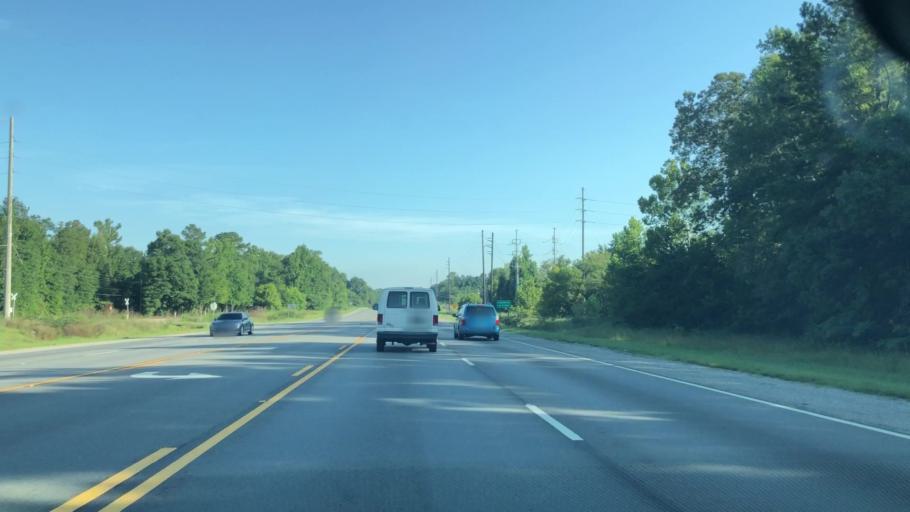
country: US
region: Alabama
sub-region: Calhoun County
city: Bynum
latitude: 33.5996
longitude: -85.9261
